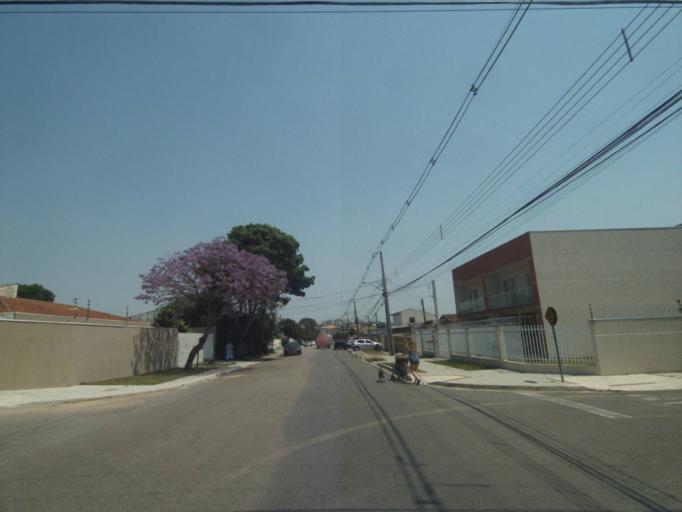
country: BR
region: Parana
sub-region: Sao Jose Dos Pinhais
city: Sao Jose dos Pinhais
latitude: -25.5116
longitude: -49.2704
